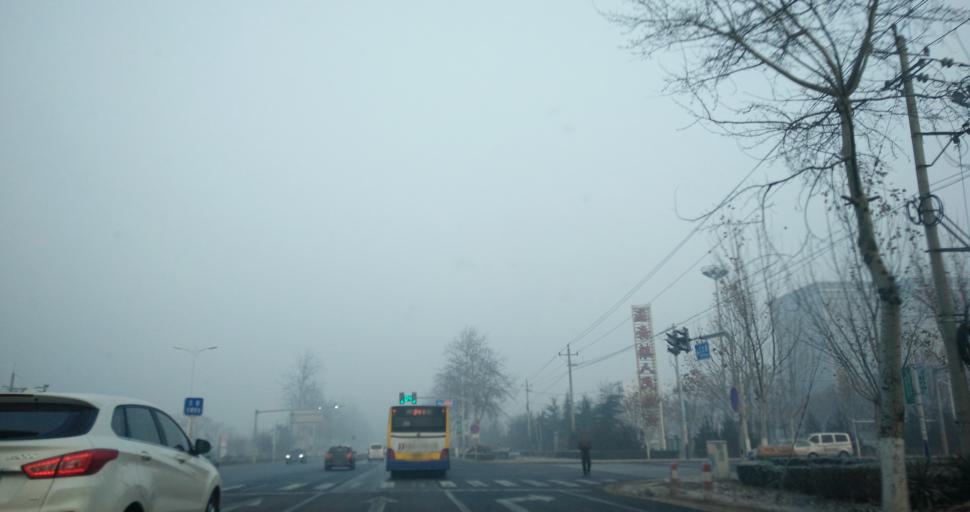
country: CN
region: Beijing
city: Yinghai
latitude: 39.7542
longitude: 116.4451
